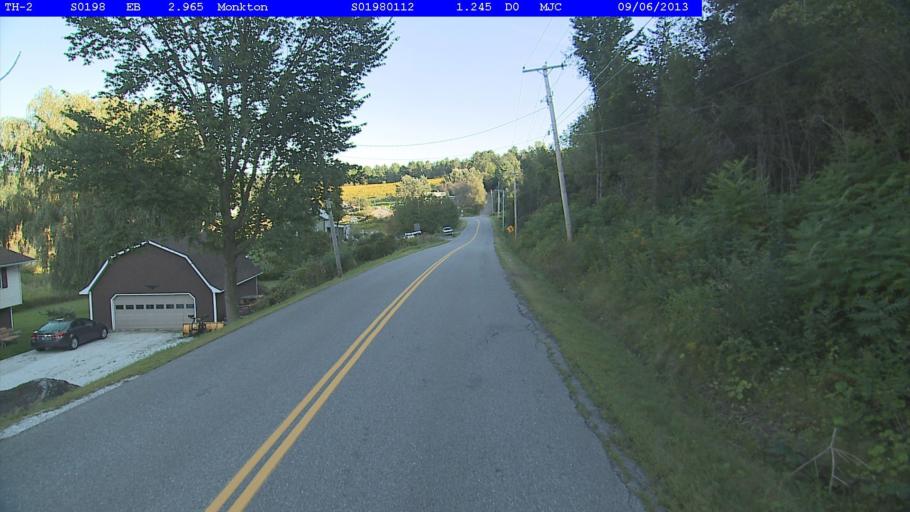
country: US
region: Vermont
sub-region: Chittenden County
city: Hinesburg
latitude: 44.2485
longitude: -73.1742
